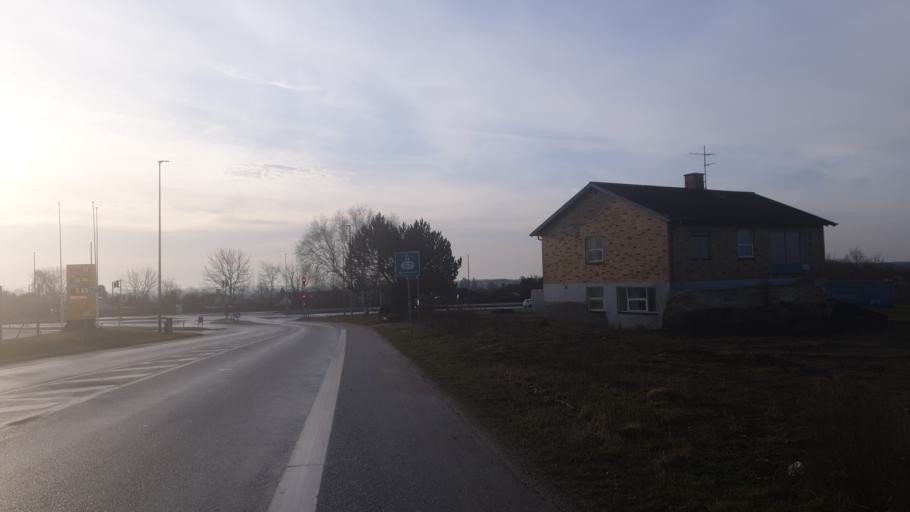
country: DK
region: Central Jutland
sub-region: Hedensted Kommune
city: Hedensted
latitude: 55.7775
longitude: 9.7107
